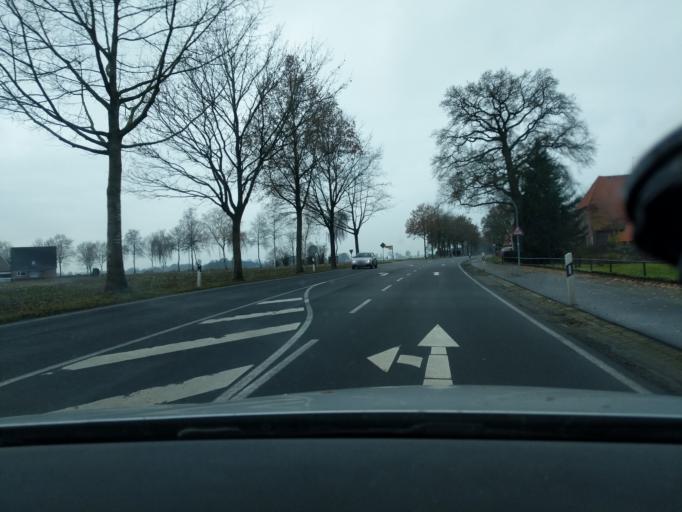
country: DE
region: Lower Saxony
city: Harsefeld
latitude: 53.4046
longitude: 9.5071
